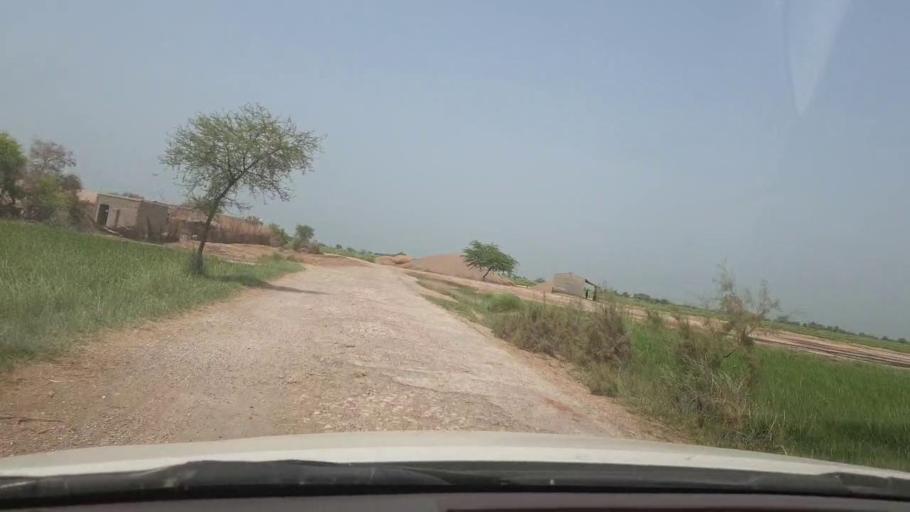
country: PK
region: Sindh
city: Shikarpur
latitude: 28.0720
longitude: 68.5751
